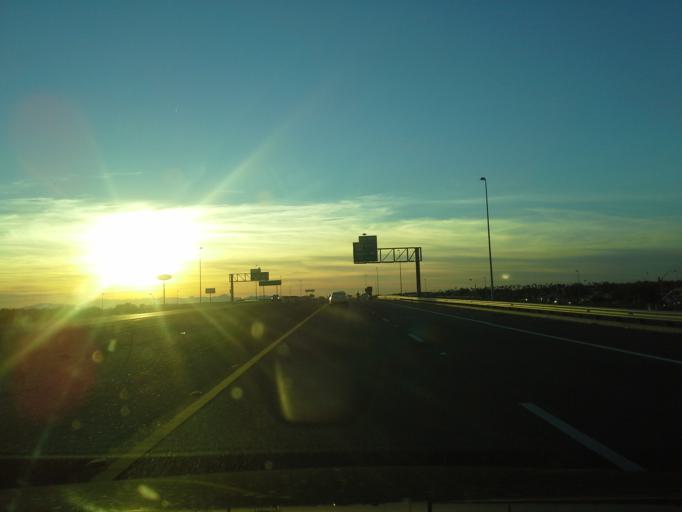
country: US
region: Arizona
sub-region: Pinal County
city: Apache Junction
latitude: 33.3867
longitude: -111.5273
